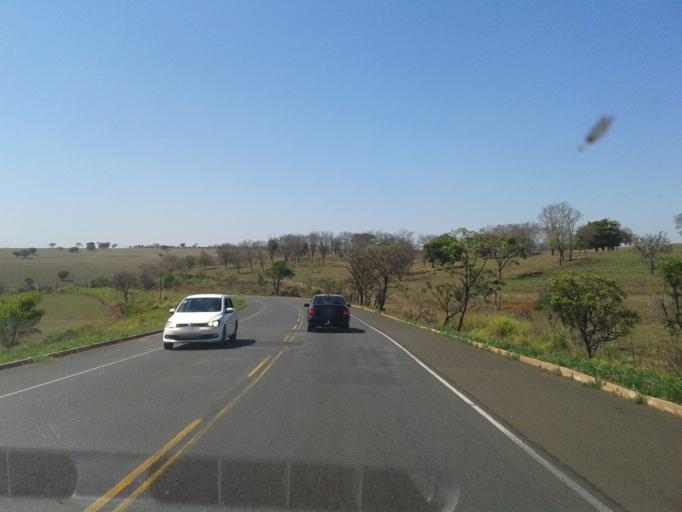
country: BR
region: Minas Gerais
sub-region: Uberlandia
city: Uberlandia
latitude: -19.0718
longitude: -48.0272
